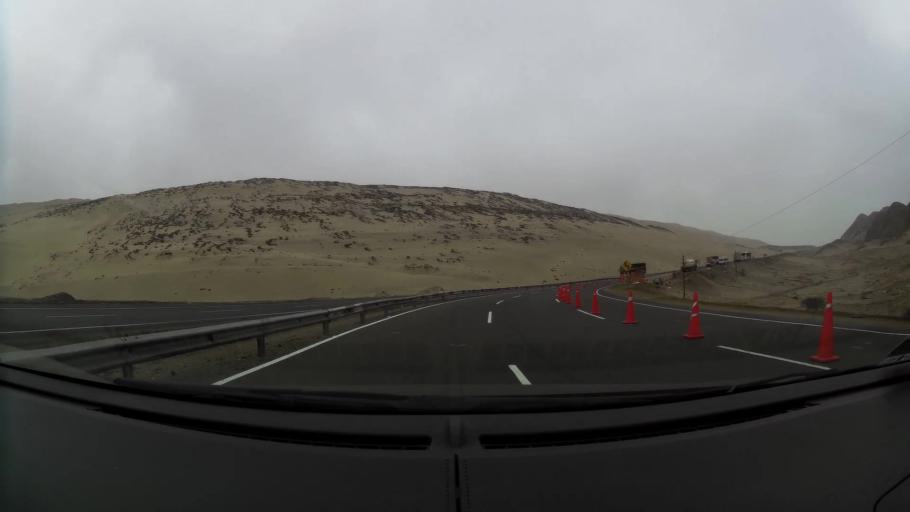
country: PE
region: La Libertad
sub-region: Viru
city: Chao
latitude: -8.7075
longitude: -78.6396
